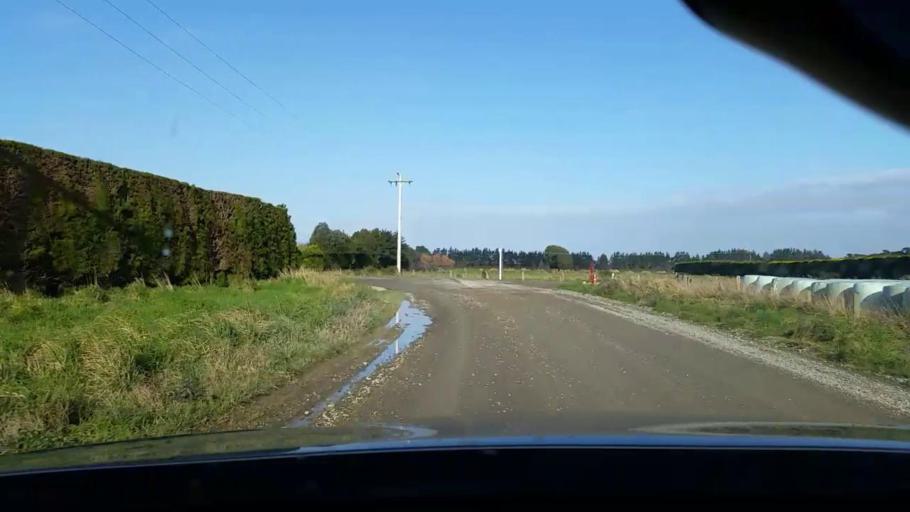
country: NZ
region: Southland
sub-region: Invercargill City
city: Invercargill
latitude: -46.2940
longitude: 168.2949
